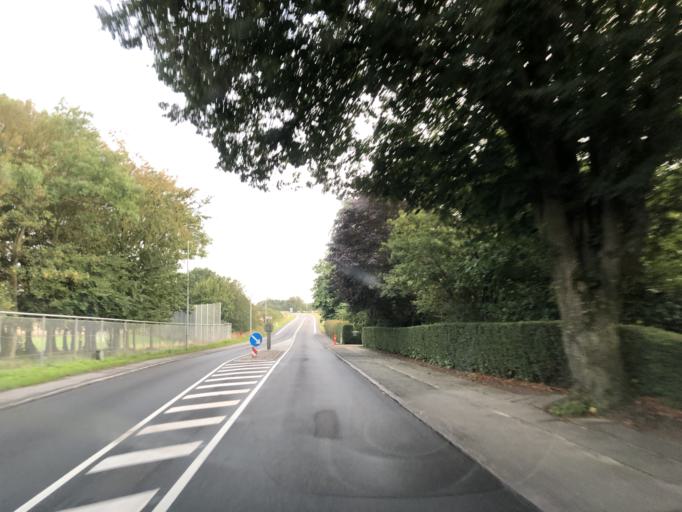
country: DK
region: Central Jutland
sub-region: Holstebro Kommune
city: Vinderup
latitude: 56.6096
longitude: 8.8792
